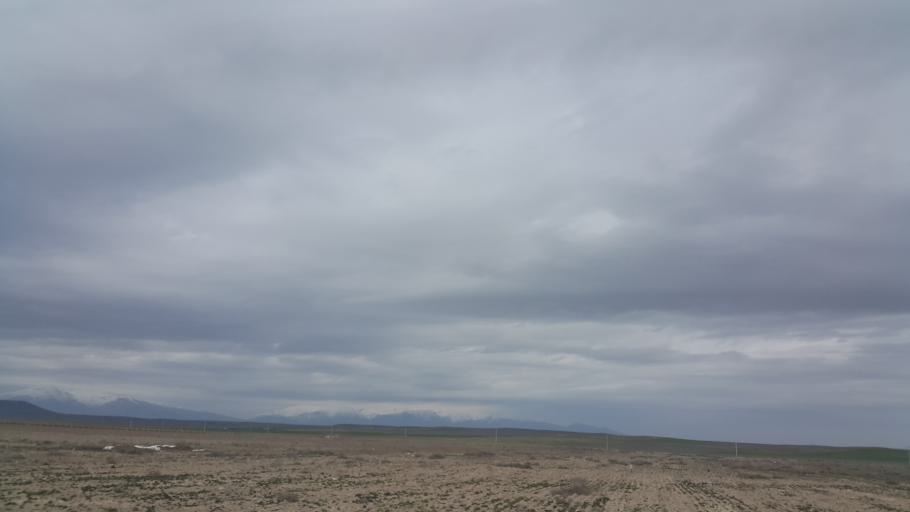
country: TR
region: Nigde
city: Altunhisar
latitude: 37.8526
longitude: 34.1736
